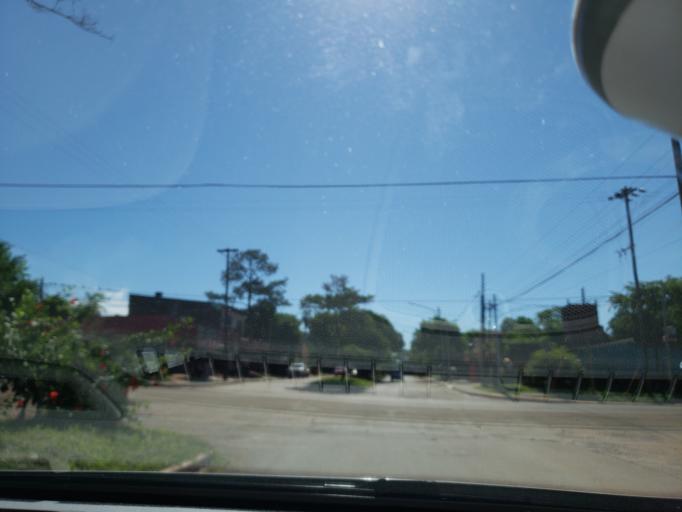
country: AR
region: Misiones
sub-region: Departamento de Capital
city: Posadas
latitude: -27.3843
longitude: -55.9300
